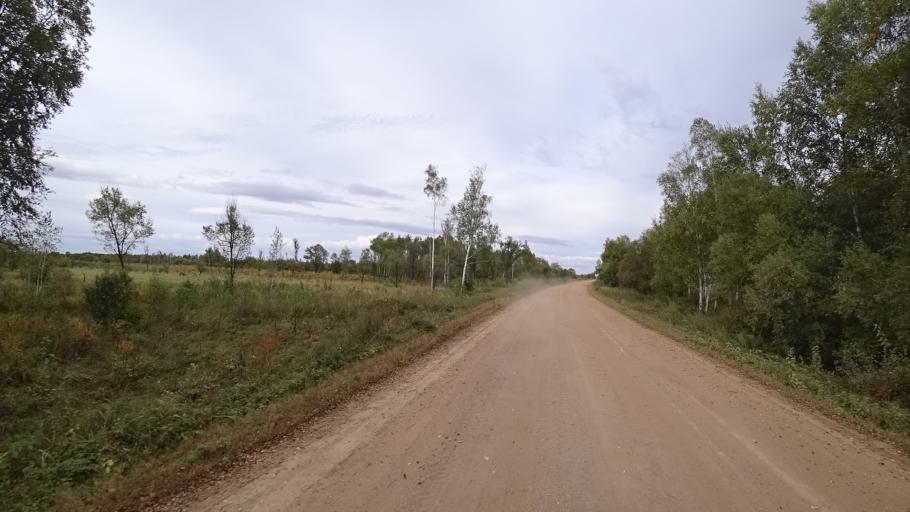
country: RU
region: Amur
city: Arkhara
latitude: 49.3418
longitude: 130.1125
